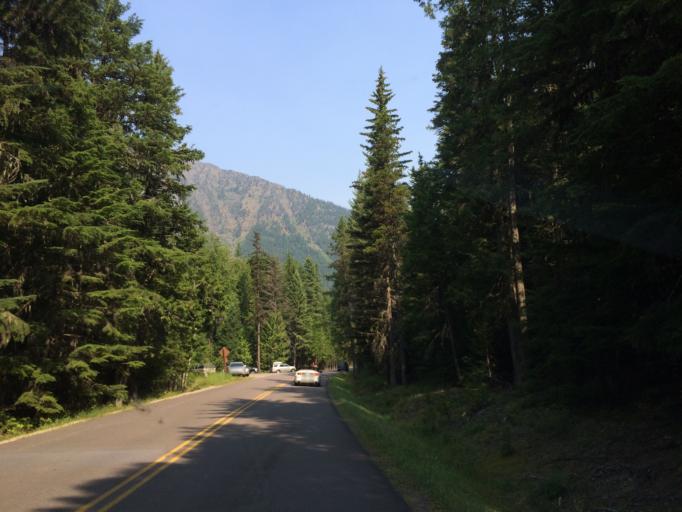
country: US
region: Montana
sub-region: Flathead County
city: Columbia Falls
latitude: 48.6342
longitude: -113.8629
